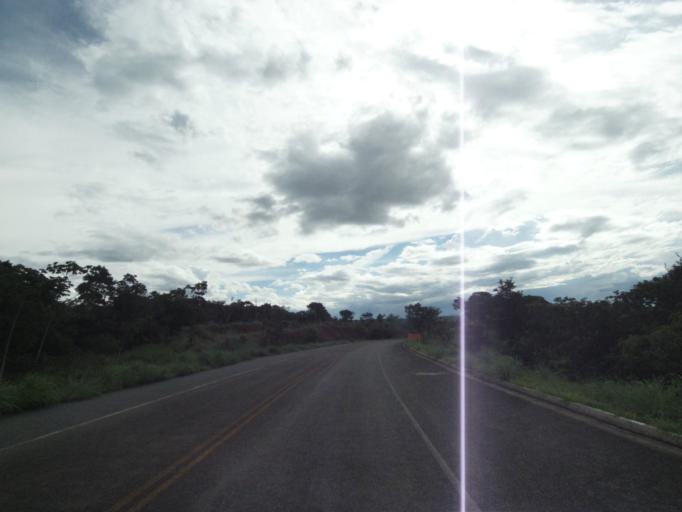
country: BR
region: Goias
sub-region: Jaragua
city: Jaragua
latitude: -15.8427
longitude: -49.3285
